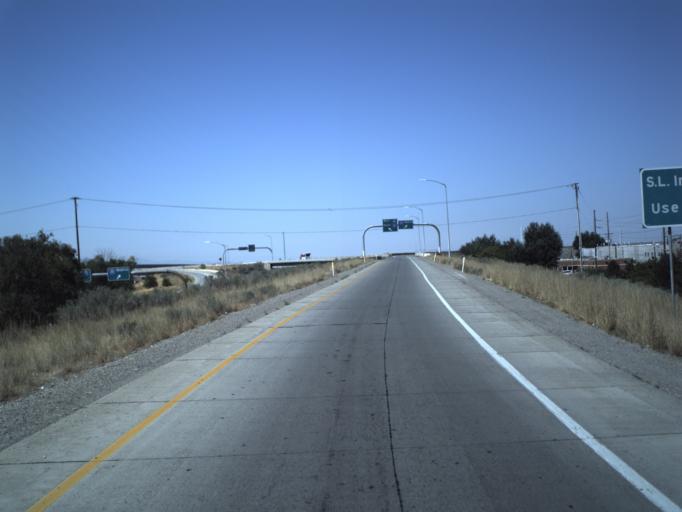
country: US
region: Utah
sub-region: Salt Lake County
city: Salt Lake City
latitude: 40.7668
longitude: -111.9416
